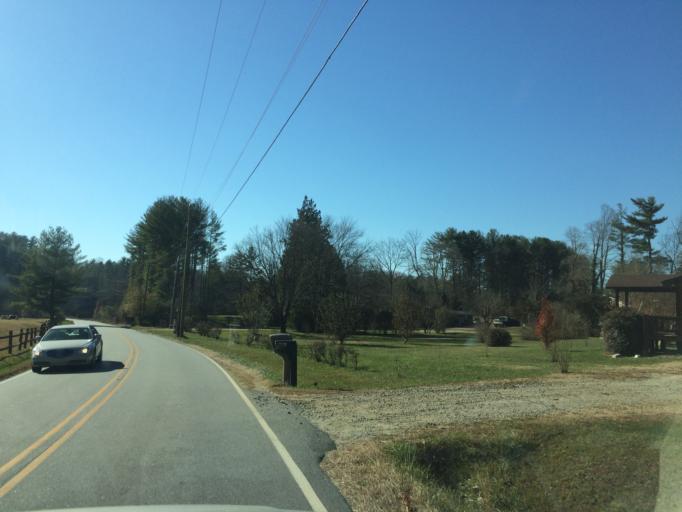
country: US
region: North Carolina
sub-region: Henderson County
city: Mountain Home
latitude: 35.3657
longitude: -82.5266
